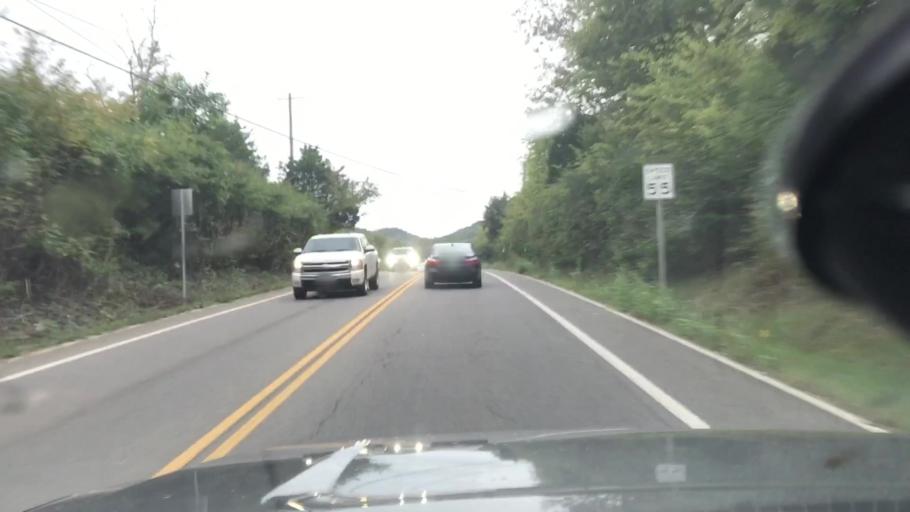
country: US
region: Tennessee
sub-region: Davidson County
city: Forest Hills
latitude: 36.0402
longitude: -86.8689
